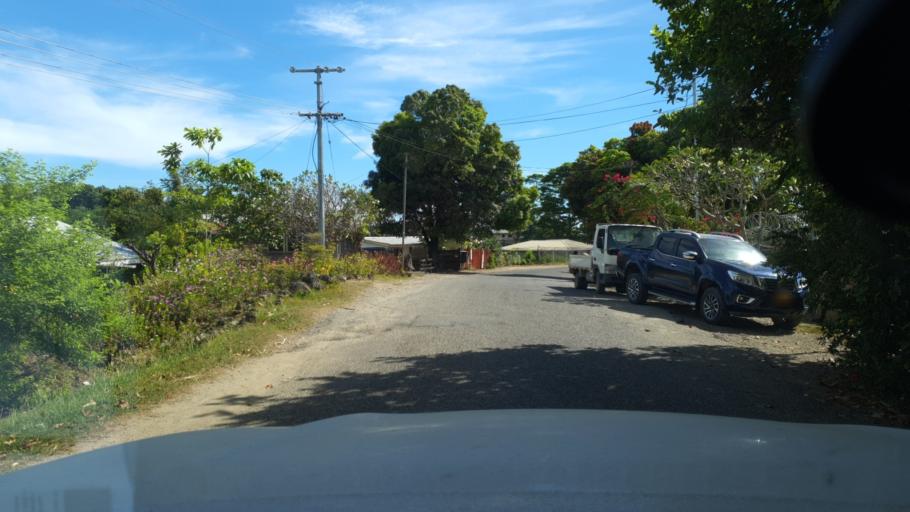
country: SB
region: Guadalcanal
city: Honiara
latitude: -9.4363
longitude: 159.9517
